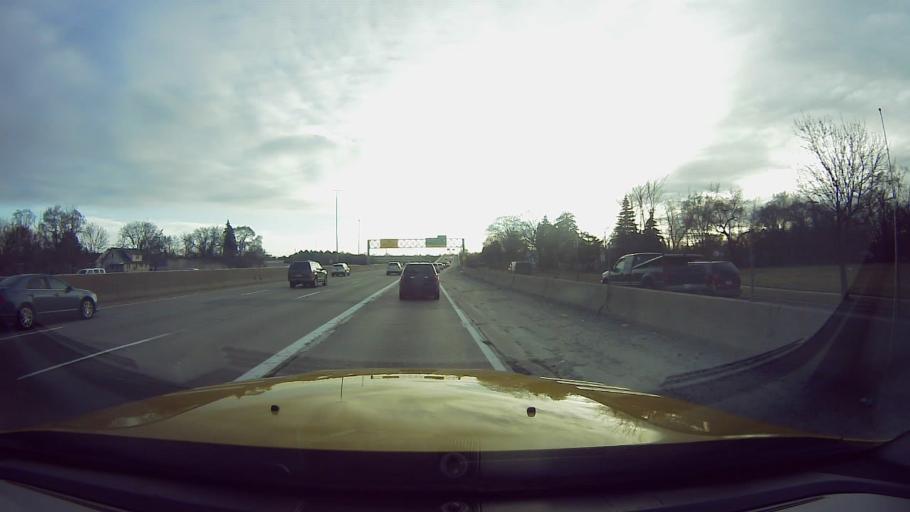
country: US
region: Michigan
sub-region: Wayne County
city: Allen Park
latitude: 42.2730
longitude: -83.2214
